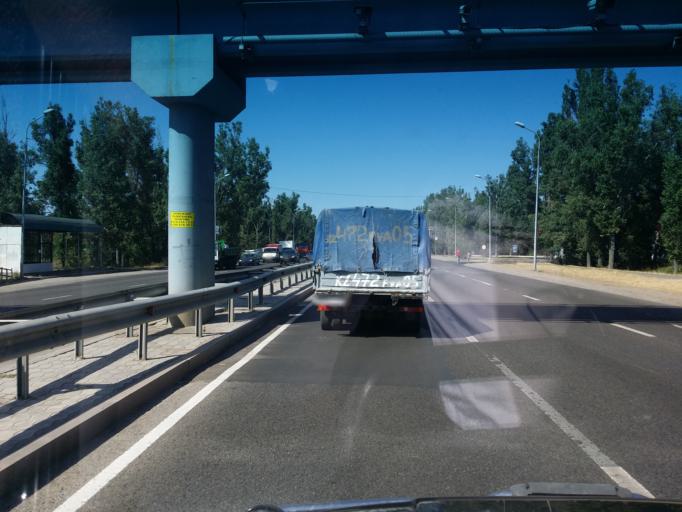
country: KZ
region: Almaty Qalasy
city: Almaty
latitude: 43.3067
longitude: 76.8975
